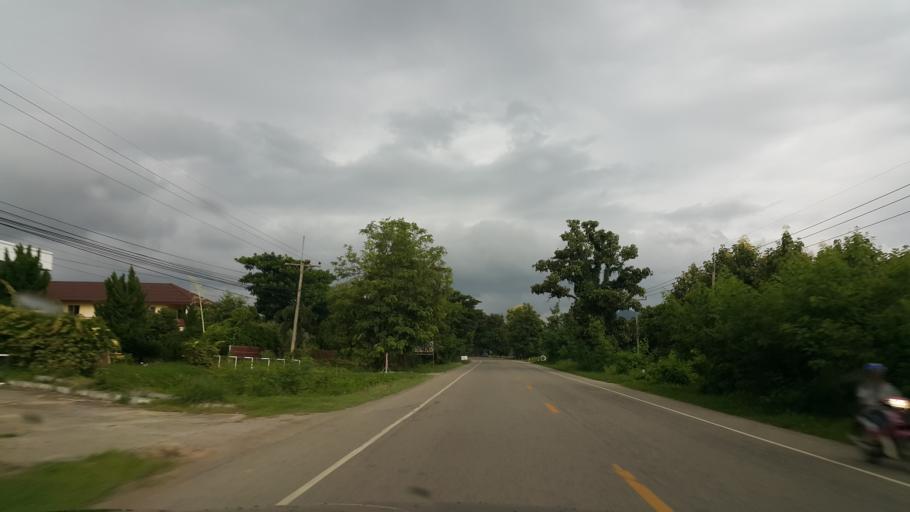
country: TH
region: Phayao
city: Dok Kham Tai
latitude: 19.2284
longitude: 100.0475
